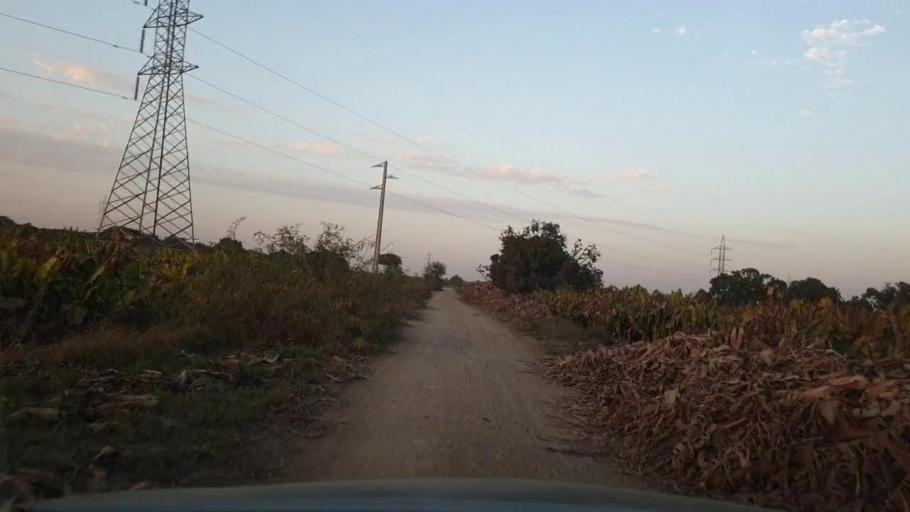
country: PK
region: Sindh
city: Matiari
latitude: 25.6167
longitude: 68.4846
